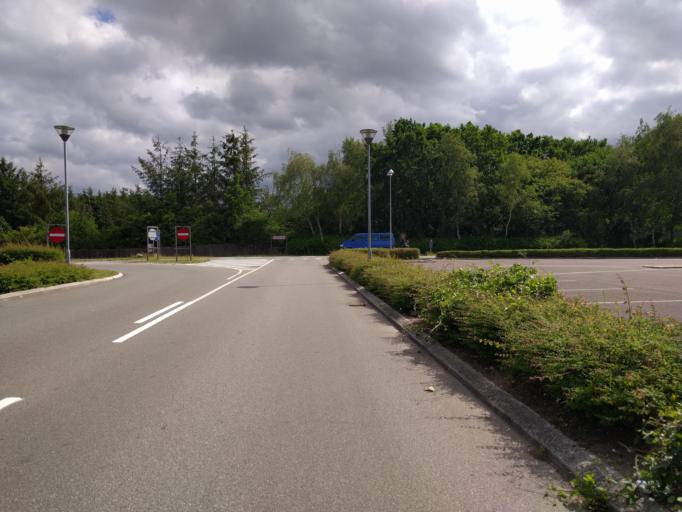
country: DK
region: South Denmark
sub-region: Odense Kommune
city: Seden
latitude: 55.4060
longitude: 10.4411
